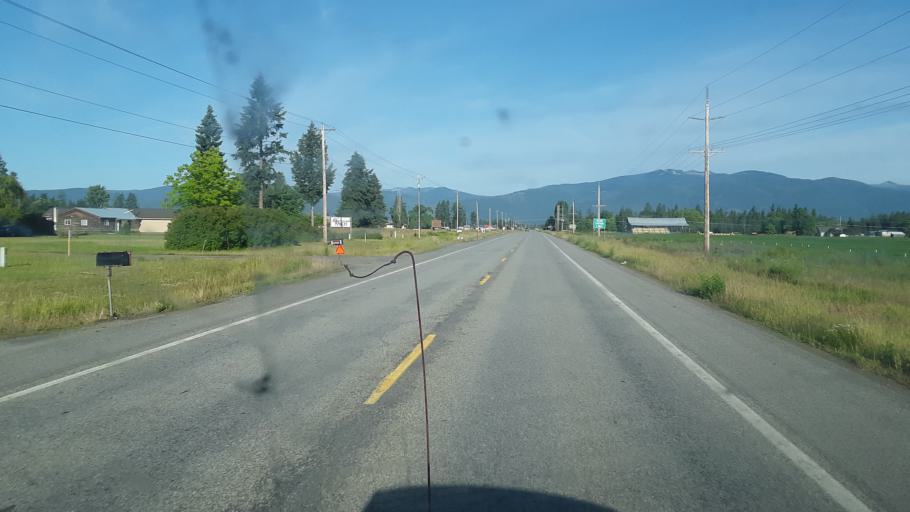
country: US
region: Idaho
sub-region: Boundary County
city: Bonners Ferry
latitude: 48.7315
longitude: -116.2690
